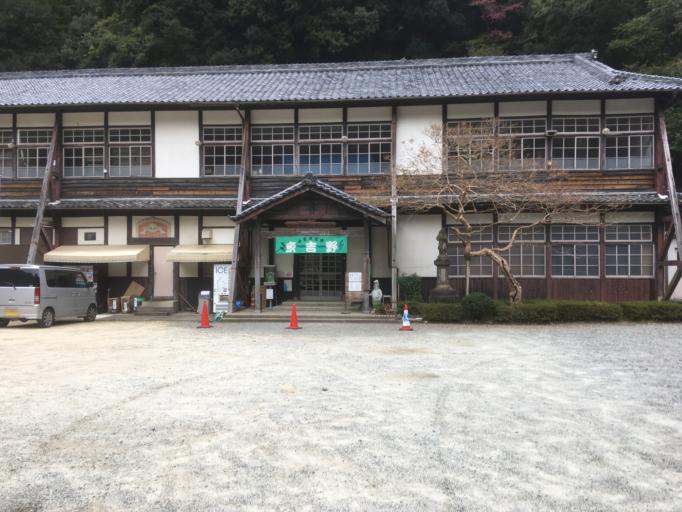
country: JP
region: Nara
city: Yoshino-cho
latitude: 34.3761
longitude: 136.0193
